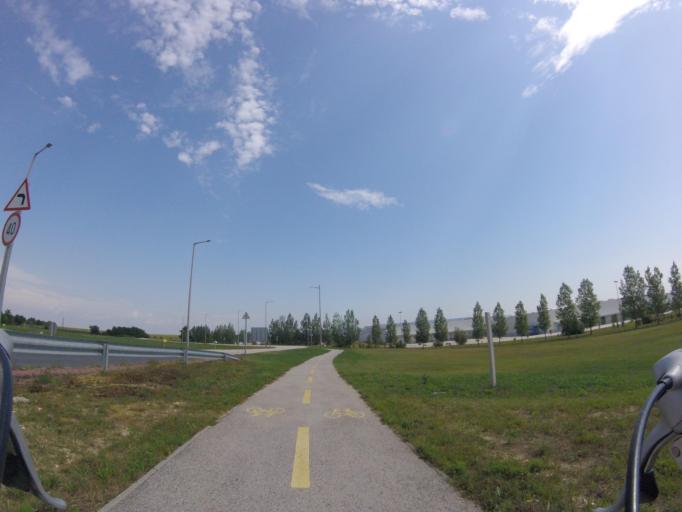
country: HU
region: Komarom-Esztergom
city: Kornye
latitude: 47.5873
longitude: 18.3219
